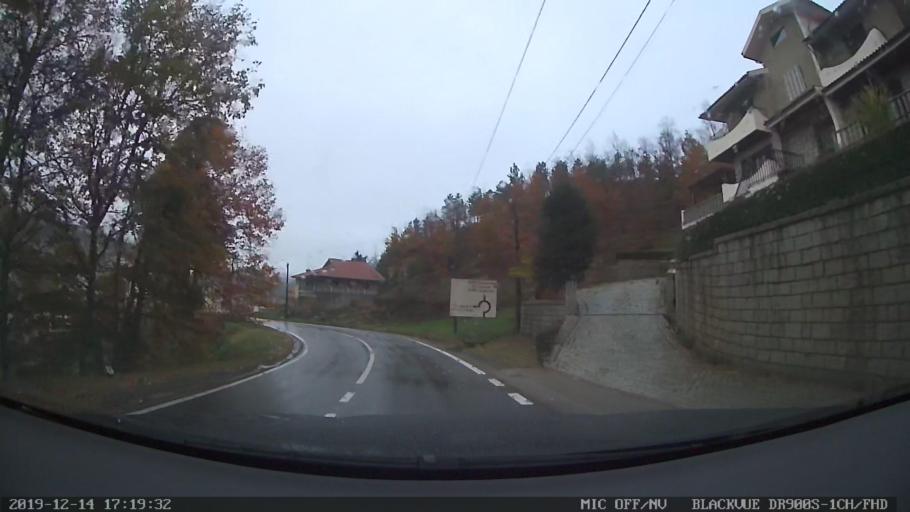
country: PT
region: Vila Real
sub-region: Vila Pouca de Aguiar
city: Vila Pouca de Aguiar
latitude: 41.4958
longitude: -7.6406
